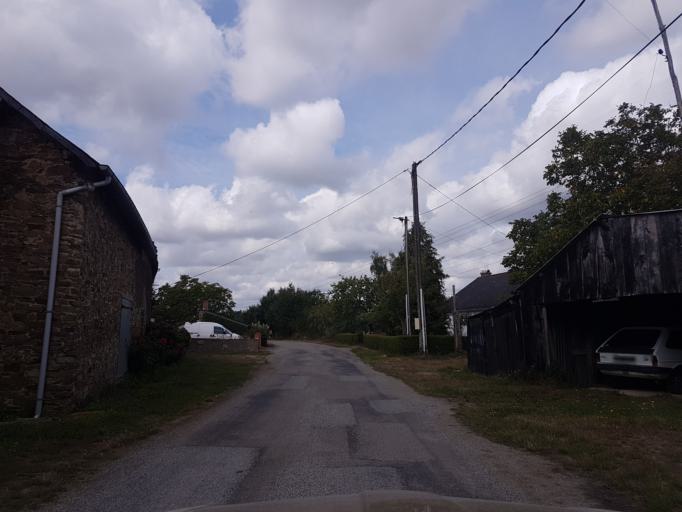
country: FR
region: Pays de la Loire
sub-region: Departement de la Loire-Atlantique
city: Petit-Mars
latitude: 47.4221
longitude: -1.4495
